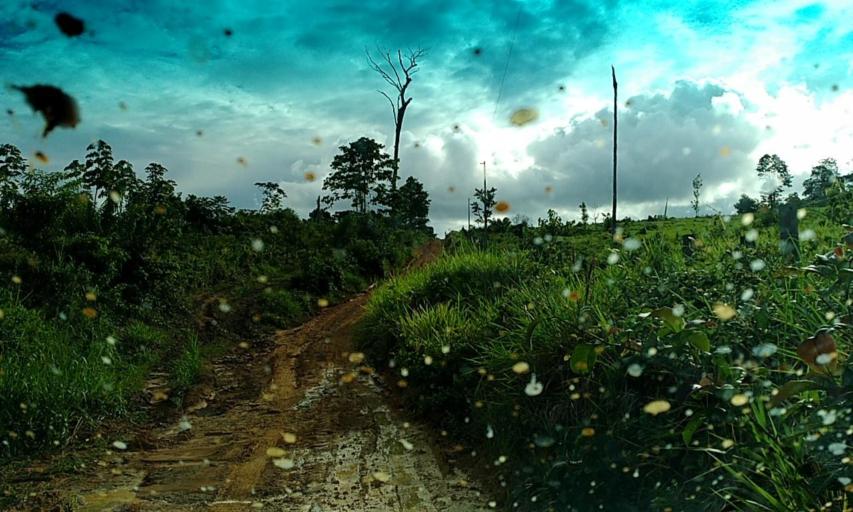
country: BR
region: Para
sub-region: Senador Jose Porfirio
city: Senador Jose Porfirio
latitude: -3.0057
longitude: -51.7427
